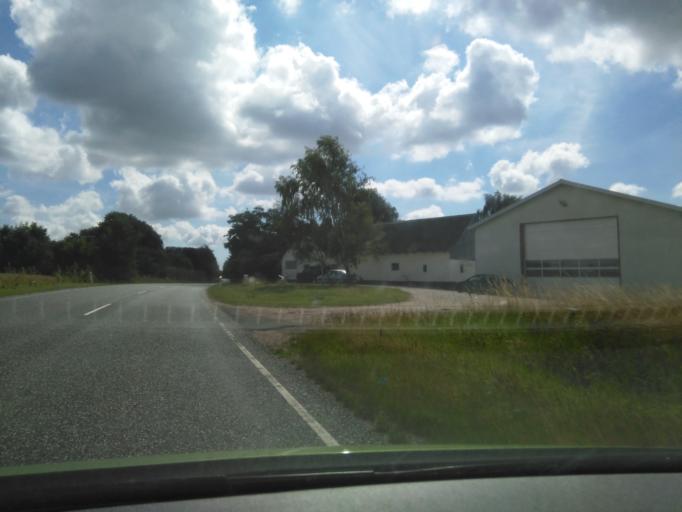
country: DK
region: Central Jutland
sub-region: Arhus Kommune
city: Solbjerg
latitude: 55.9708
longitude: 10.0691
